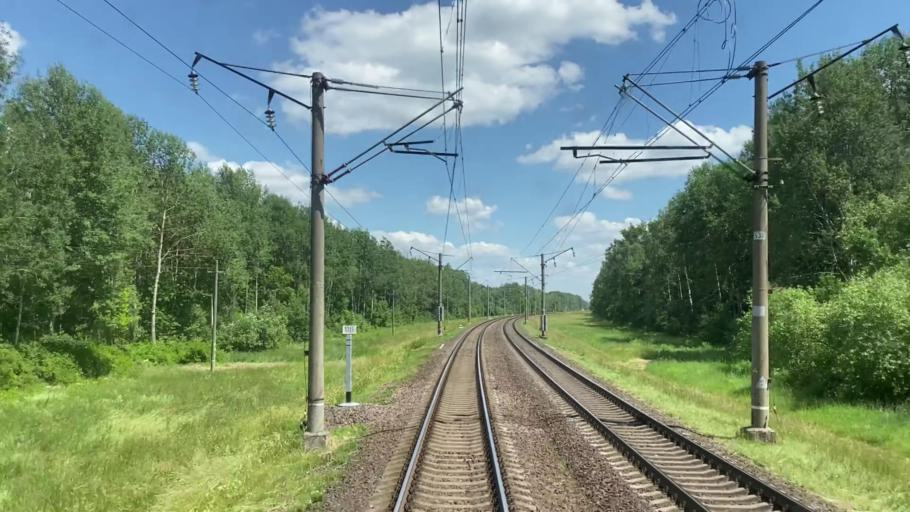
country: BY
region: Brest
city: Pruzhany
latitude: 52.5005
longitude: 24.6196
